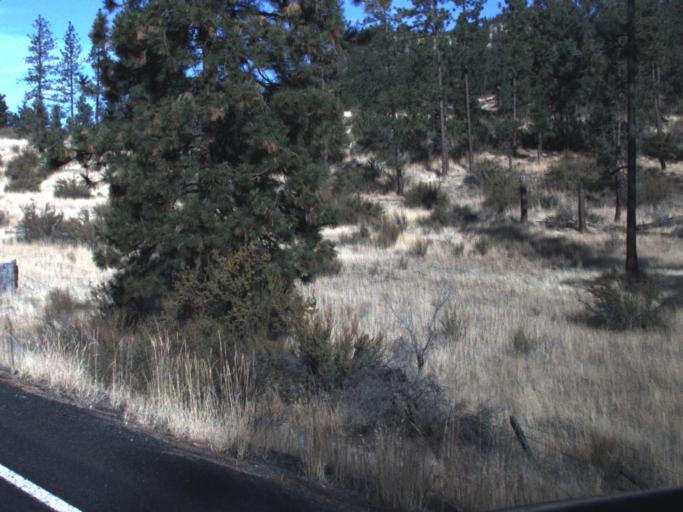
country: US
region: Washington
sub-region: Lincoln County
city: Davenport
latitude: 47.8985
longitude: -118.2742
